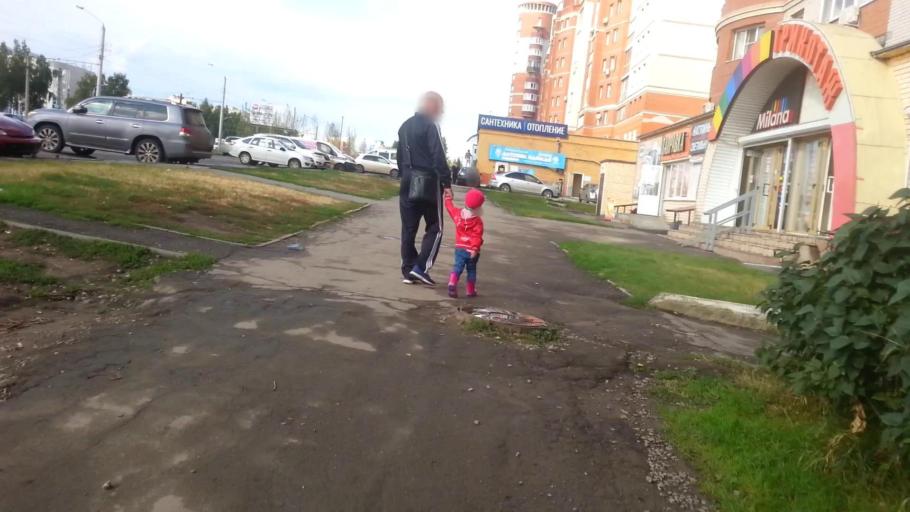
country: RU
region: Altai Krai
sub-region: Gorod Barnaulskiy
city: Barnaul
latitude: 53.3514
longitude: 83.6983
